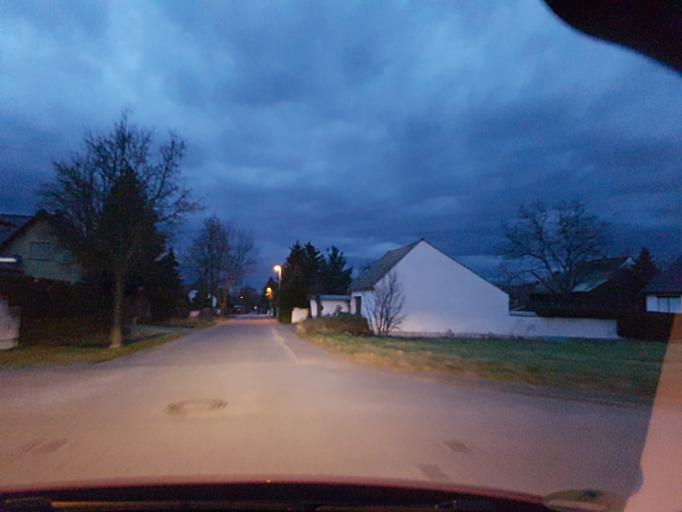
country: DE
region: Brandenburg
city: Groden
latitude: 51.4064
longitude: 13.5649
